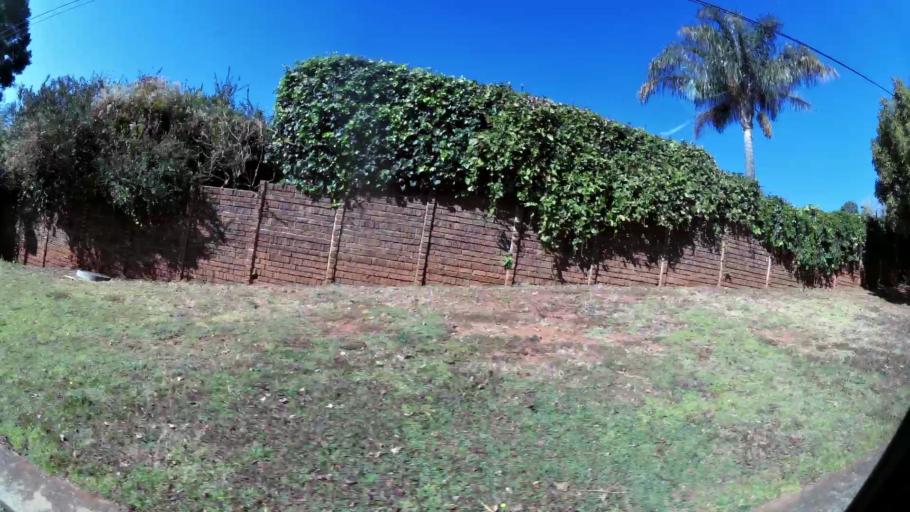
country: ZA
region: Gauteng
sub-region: City of Johannesburg Metropolitan Municipality
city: Roodepoort
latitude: -26.1211
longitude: 27.8710
